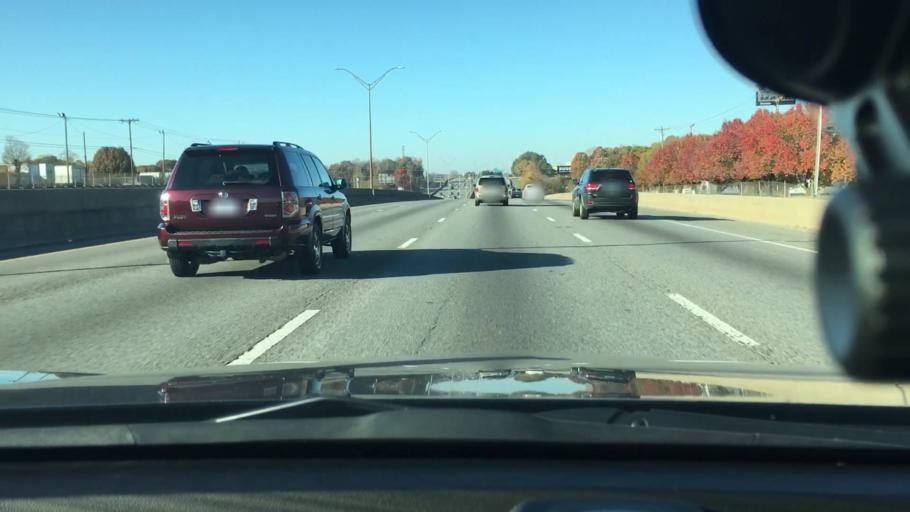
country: US
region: North Carolina
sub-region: Mecklenburg County
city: Charlotte
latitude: 35.2755
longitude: -80.8220
